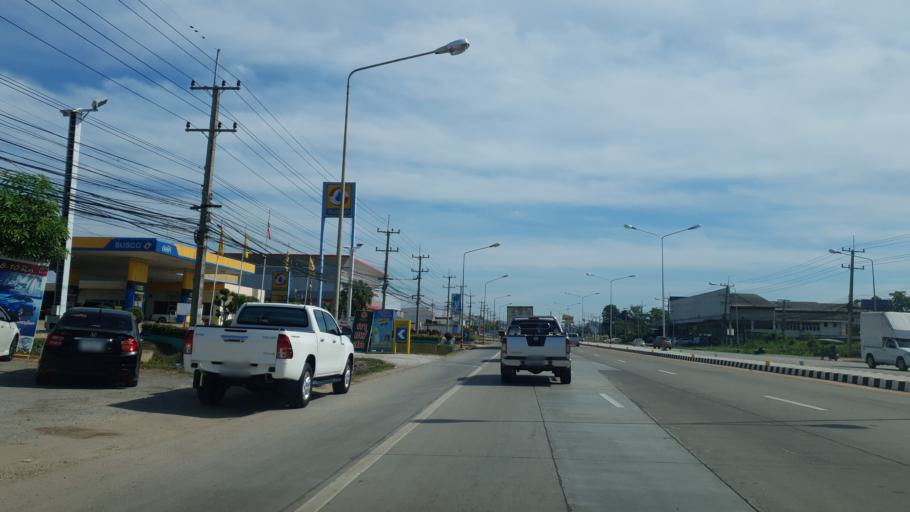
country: TH
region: Phitsanulok
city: Phitsanulok
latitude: 16.8165
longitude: 100.3075
